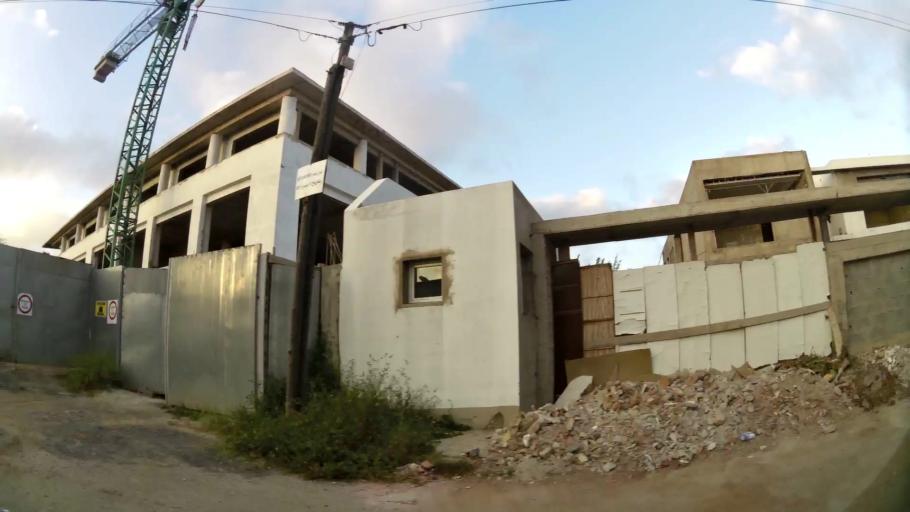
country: MA
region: Rabat-Sale-Zemmour-Zaer
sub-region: Rabat
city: Rabat
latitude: 33.9724
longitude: -6.8329
